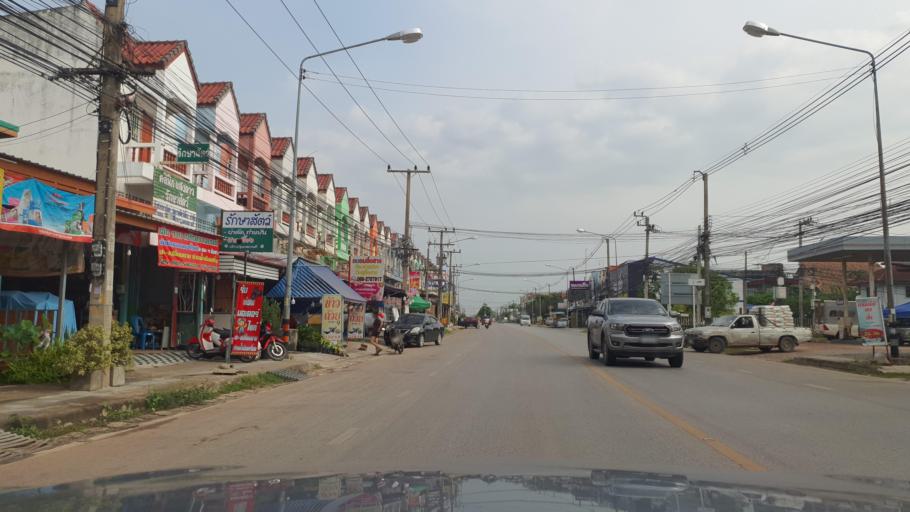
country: TH
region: Phitsanulok
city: Phitsanulok
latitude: 16.8545
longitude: 100.2538
